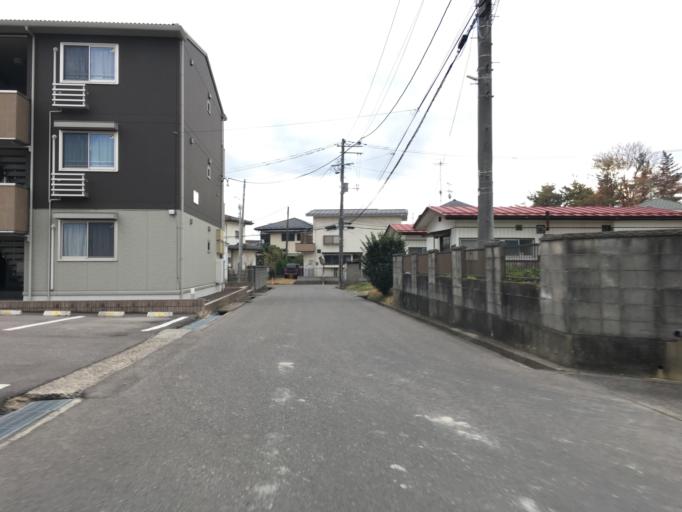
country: JP
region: Fukushima
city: Fukushima-shi
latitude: 37.8007
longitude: 140.4890
